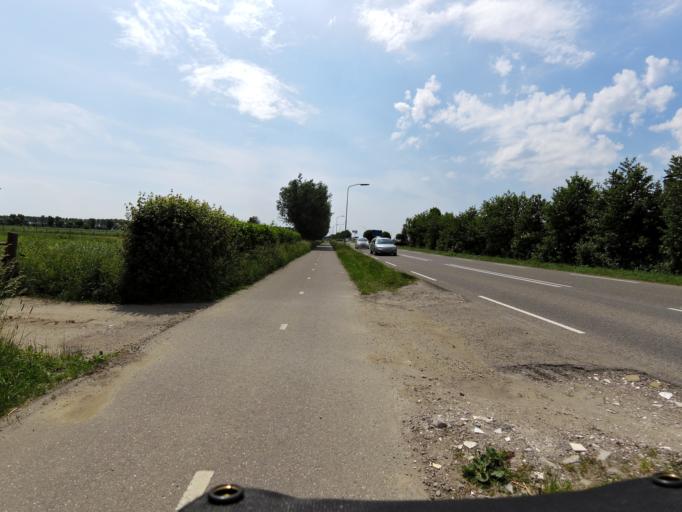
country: NL
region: North Brabant
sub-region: Gemeente Aalburg
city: Aalburg
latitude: 51.8073
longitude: 5.0871
